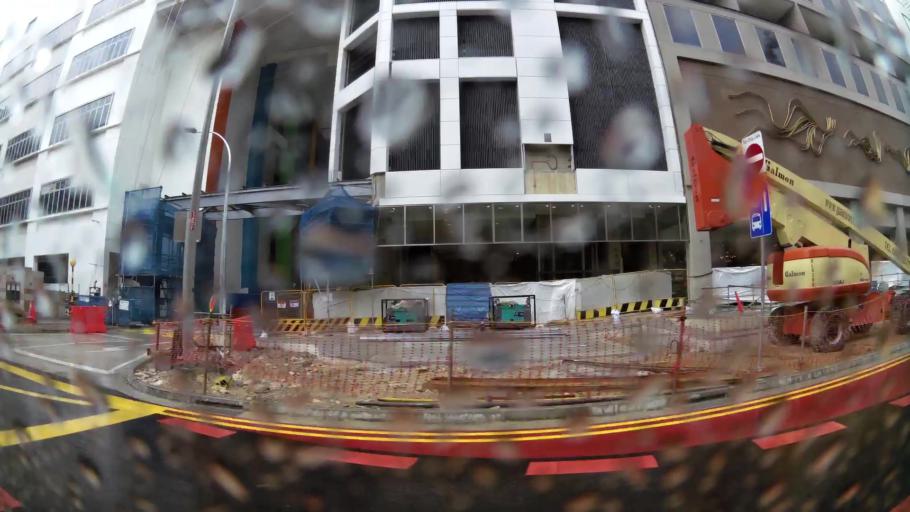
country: SG
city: Singapore
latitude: 1.2993
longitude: 103.8508
